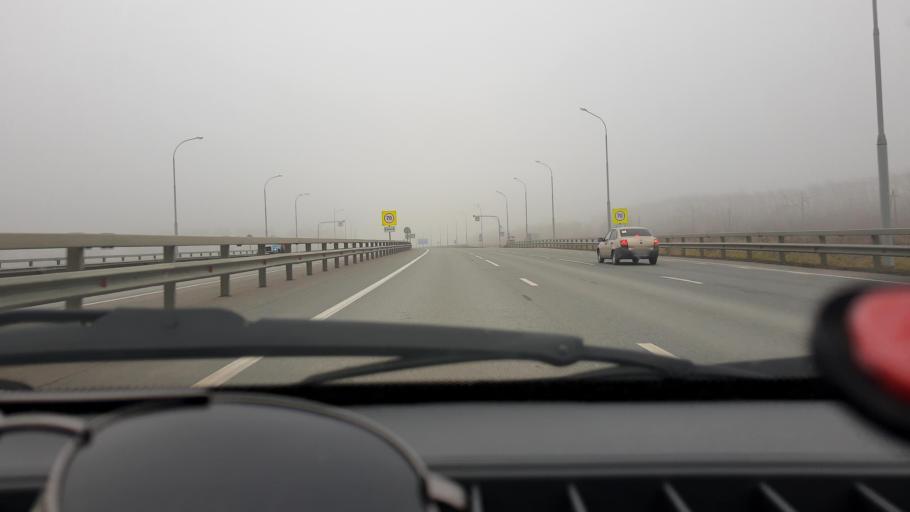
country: RU
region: Bashkortostan
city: Kabakovo
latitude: 54.6526
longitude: 56.1105
